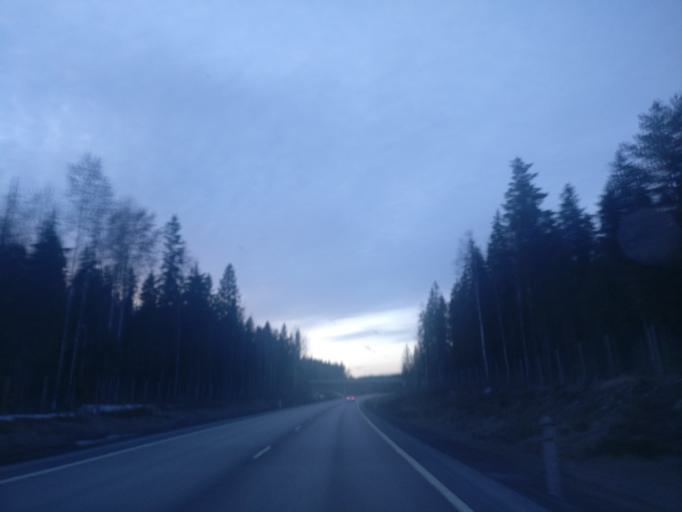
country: FI
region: Central Finland
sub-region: Jyvaeskylae
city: Saeynaetsalo
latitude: 62.1963
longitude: 25.8957
